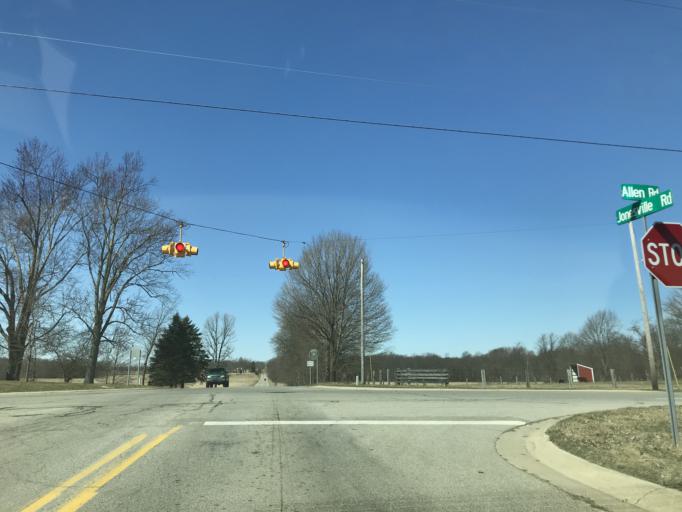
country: US
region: Michigan
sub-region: Hillsdale County
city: Litchfield
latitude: 41.9856
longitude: -84.7676
